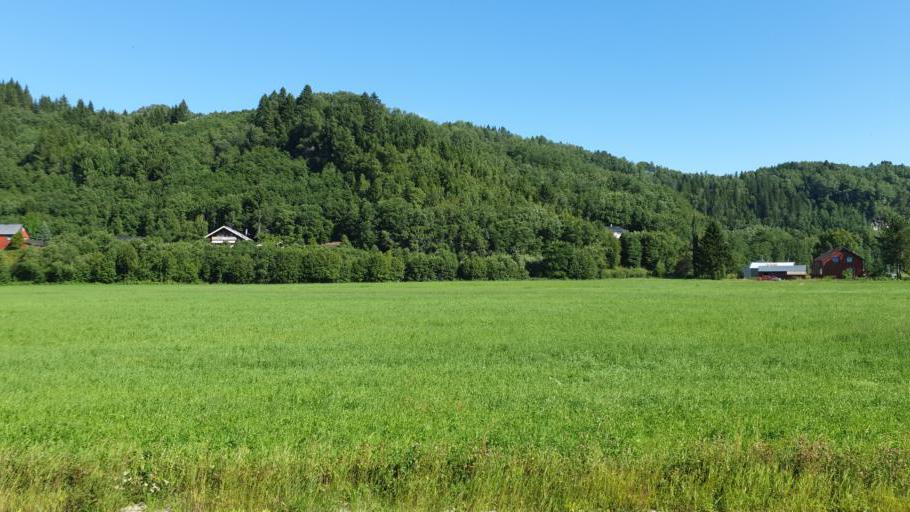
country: NO
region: Sor-Trondelag
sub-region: Orkdal
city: Orkanger
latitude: 63.2090
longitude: 9.7869
